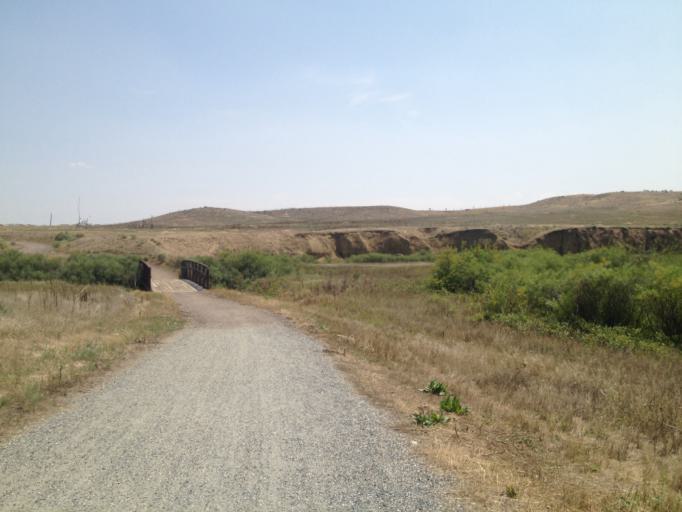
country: US
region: Colorado
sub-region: Boulder County
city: Lafayette
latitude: 39.9847
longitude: -105.0655
